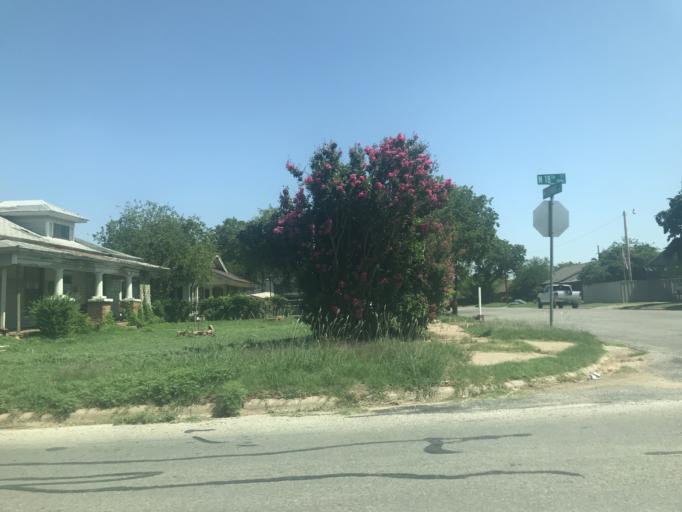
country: US
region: Texas
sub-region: Taylor County
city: Abilene
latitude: 32.4700
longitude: -99.7422
